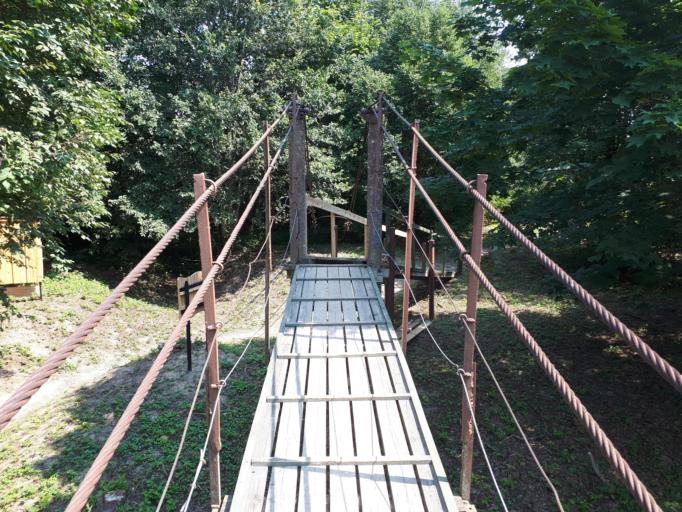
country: LT
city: Priekule
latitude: 55.5953
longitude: 21.2903
